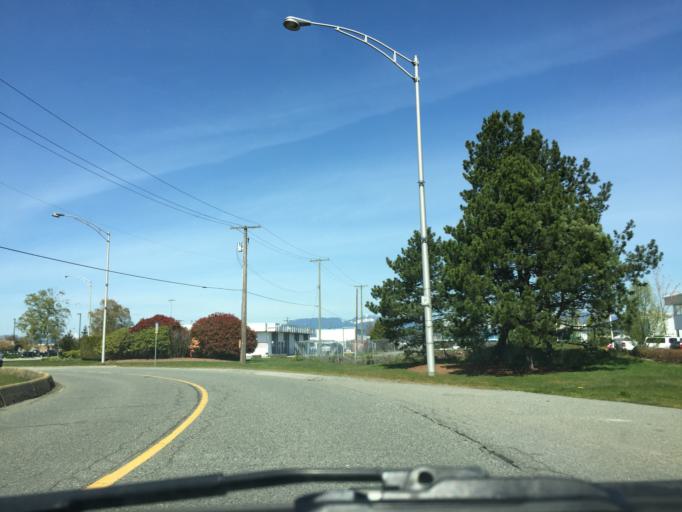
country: CA
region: British Columbia
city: Richmond
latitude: 49.1787
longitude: -123.1670
